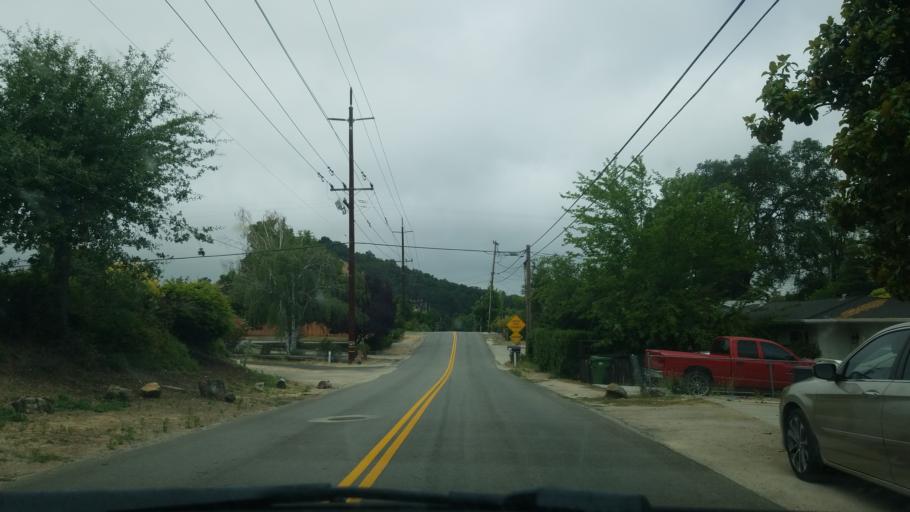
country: US
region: California
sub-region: San Luis Obispo County
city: Atascadero
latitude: 35.4638
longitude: -120.6691
